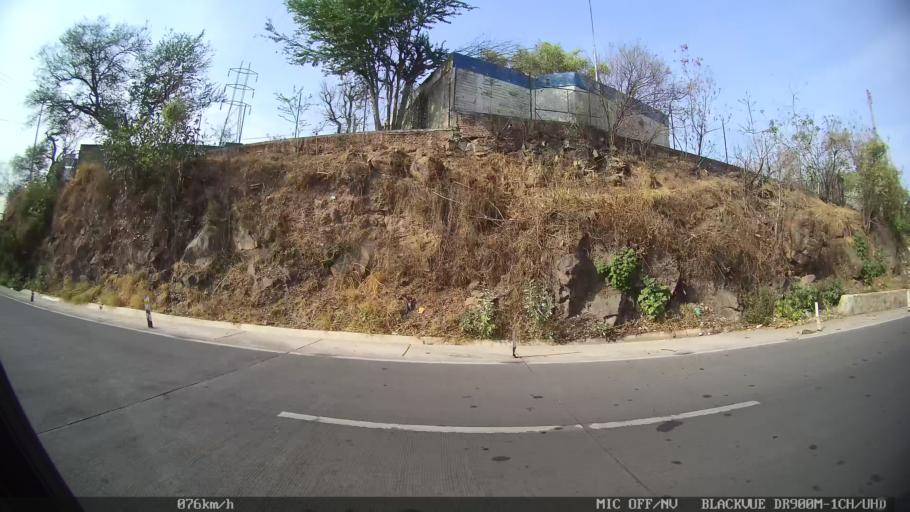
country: MX
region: Jalisco
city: Tlaquepaque
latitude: 20.7123
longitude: -103.2899
